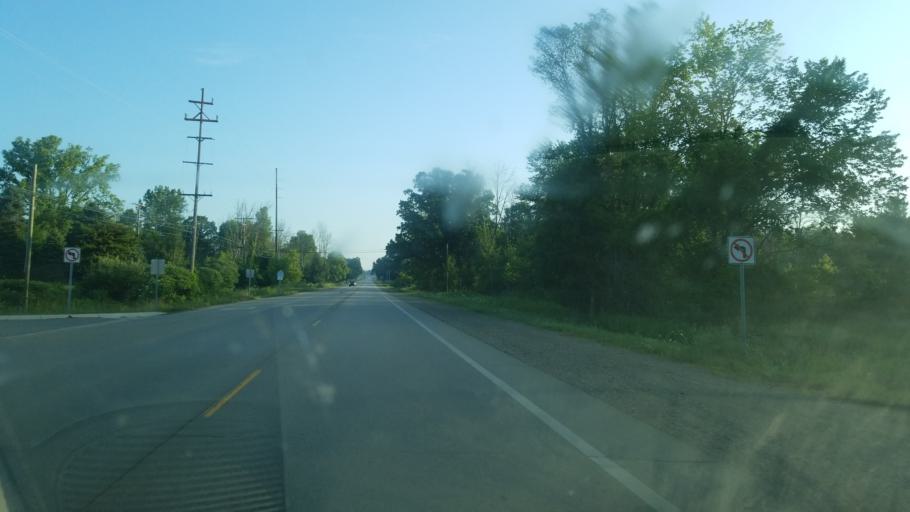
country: US
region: Michigan
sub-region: Montcalm County
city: Stanton
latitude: 43.2744
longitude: -85.0737
